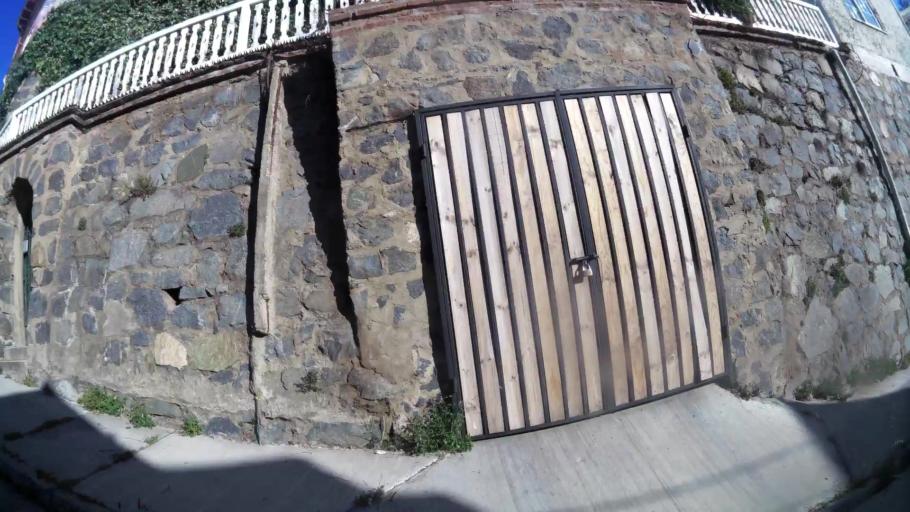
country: CL
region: Valparaiso
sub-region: Provincia de Valparaiso
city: Valparaiso
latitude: -33.0487
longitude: -71.6261
